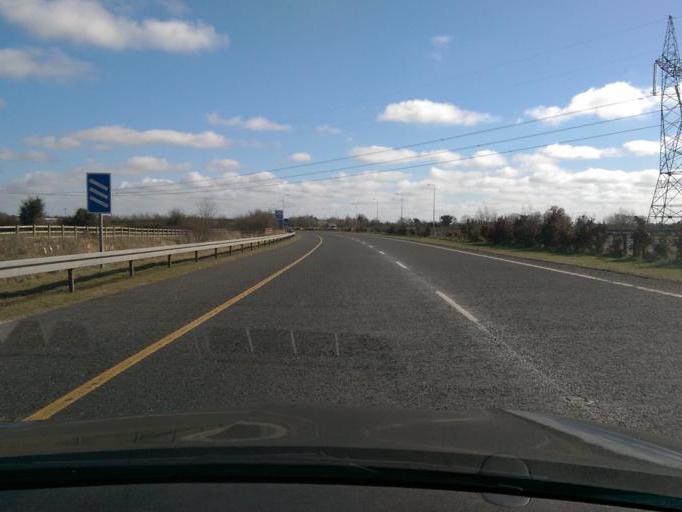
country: IE
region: Leinster
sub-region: An Mhi
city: Longwood
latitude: 53.4114
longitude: -6.8909
